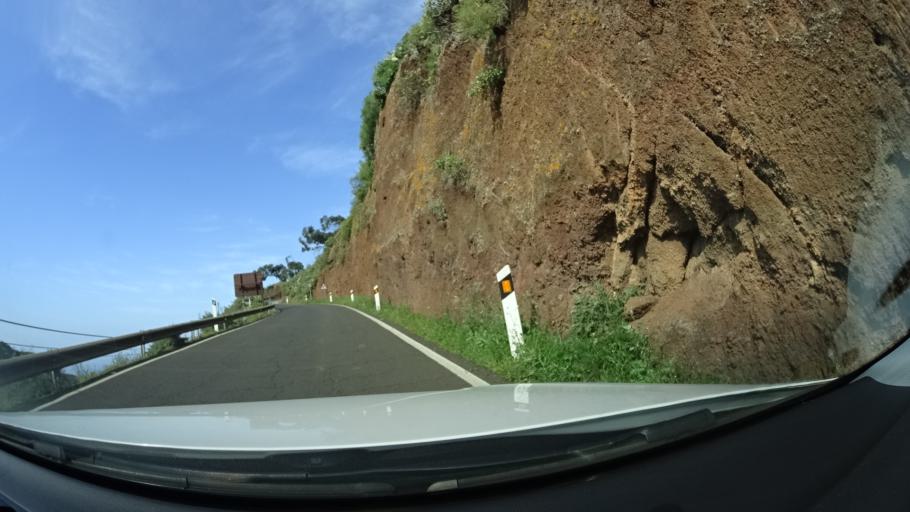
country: ES
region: Canary Islands
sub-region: Provincia de Las Palmas
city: Guia
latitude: 28.1101
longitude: -15.6390
